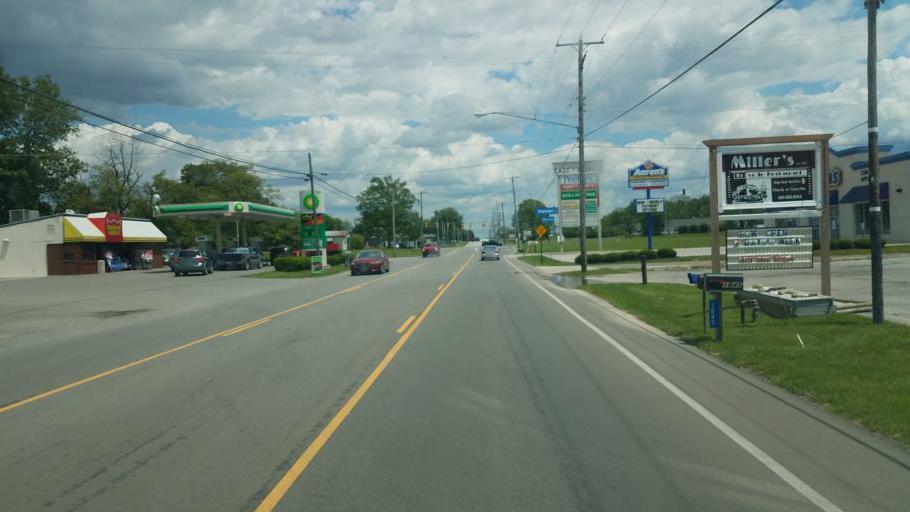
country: US
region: Ohio
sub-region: Crawford County
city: Bucyrus
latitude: 40.8125
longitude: -82.9486
